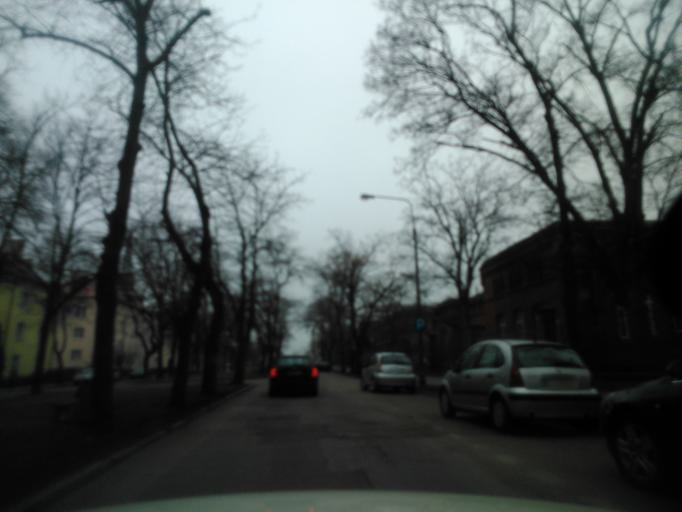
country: PL
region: Kujawsko-Pomorskie
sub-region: Torun
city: Torun
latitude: 53.0126
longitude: 18.6172
